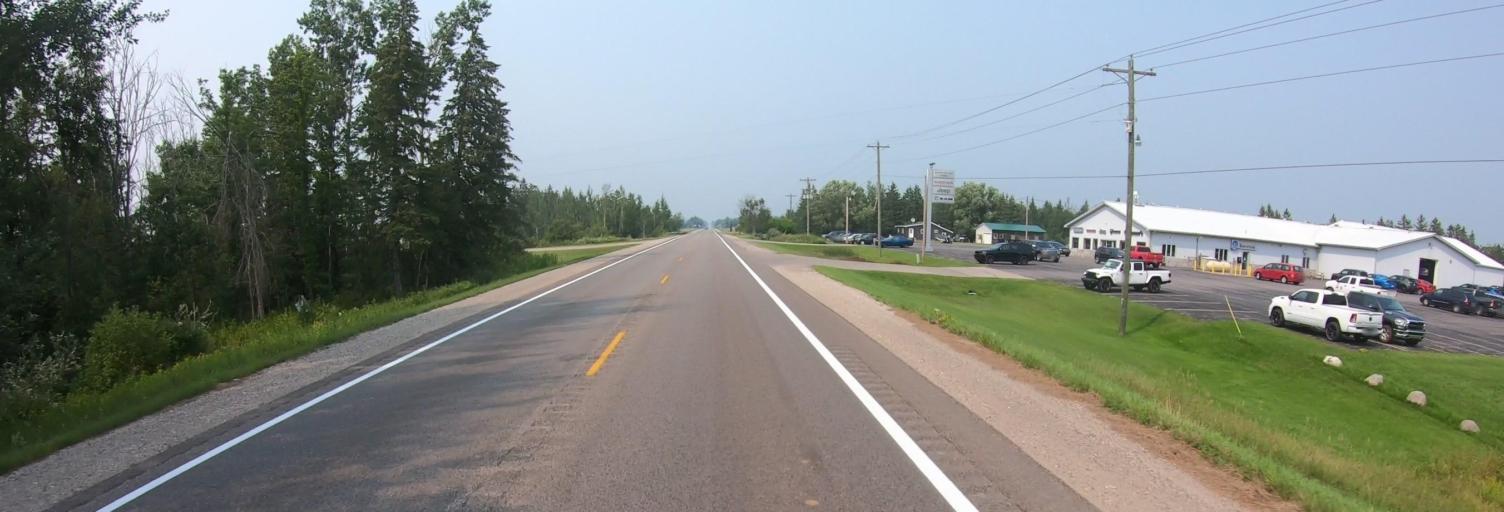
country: US
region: Michigan
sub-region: Chippewa County
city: Sault Ste. Marie
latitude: 46.1787
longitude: -84.3635
